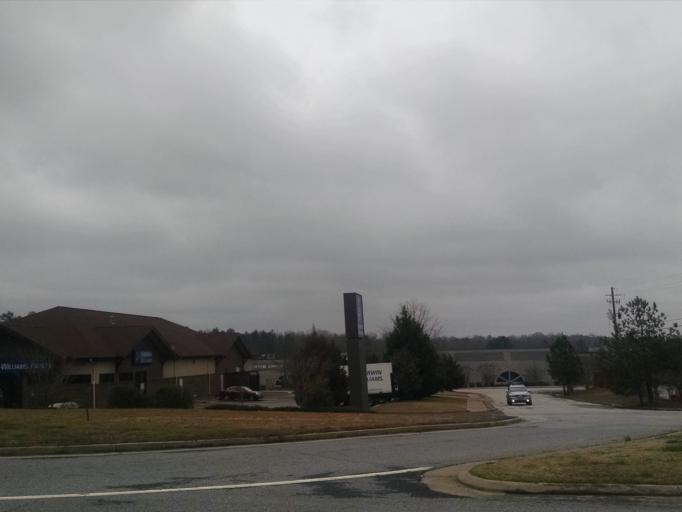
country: US
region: Georgia
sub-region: Gwinnett County
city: Sugar Hill
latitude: 34.1025
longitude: -84.0223
